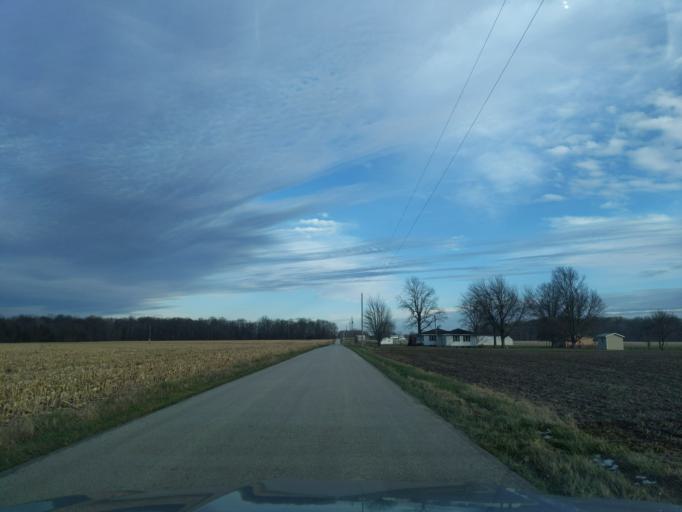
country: US
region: Indiana
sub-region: Decatur County
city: Westport
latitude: 39.2193
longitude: -85.4971
